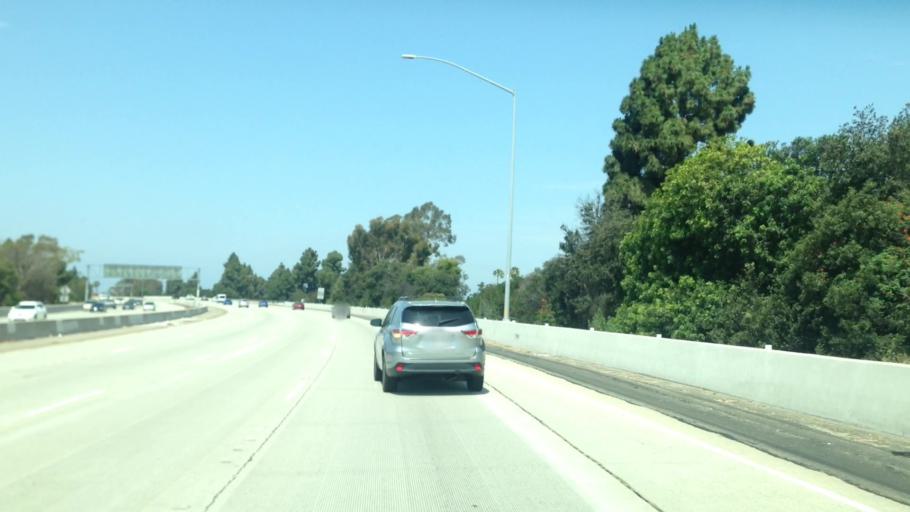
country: US
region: California
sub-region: Los Angeles County
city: Ladera Heights
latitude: 33.9885
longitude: -118.4064
